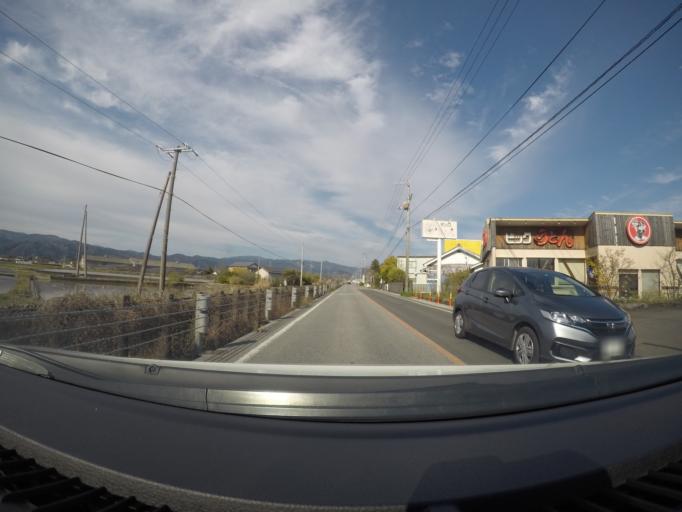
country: JP
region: Kochi
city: Kochi-shi
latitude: 33.5951
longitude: 133.6667
